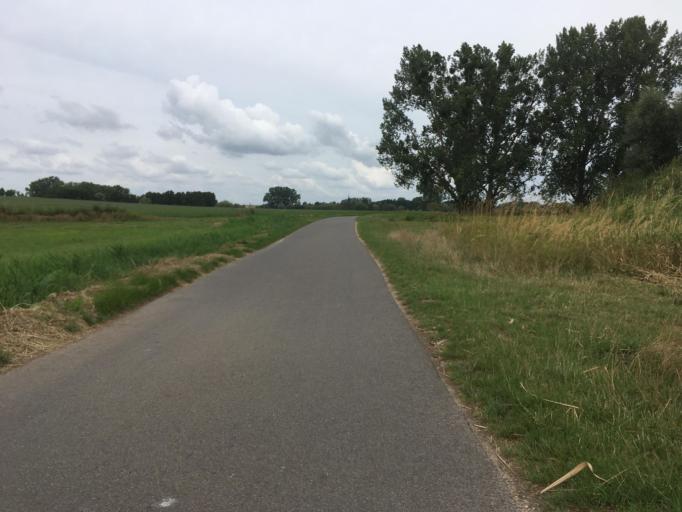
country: DE
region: Brandenburg
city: Prenzlau
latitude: 53.2675
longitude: 13.8474
